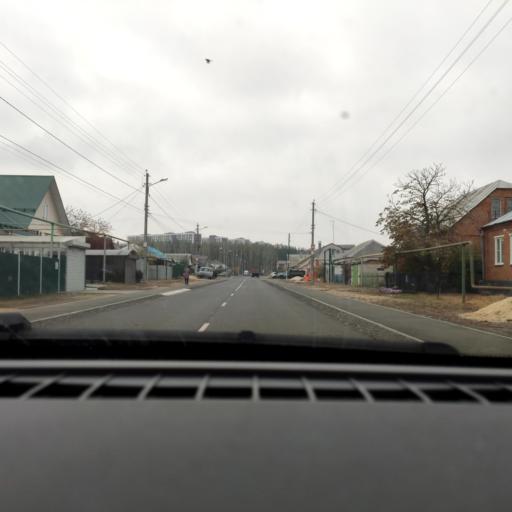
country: RU
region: Voronezj
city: Somovo
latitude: 51.7455
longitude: 39.3253
